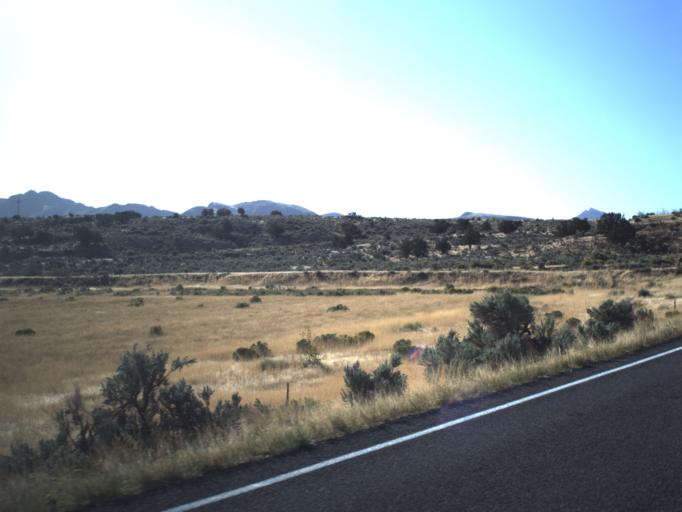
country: US
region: Utah
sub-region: Millard County
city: Delta
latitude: 39.5192
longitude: -112.2733
